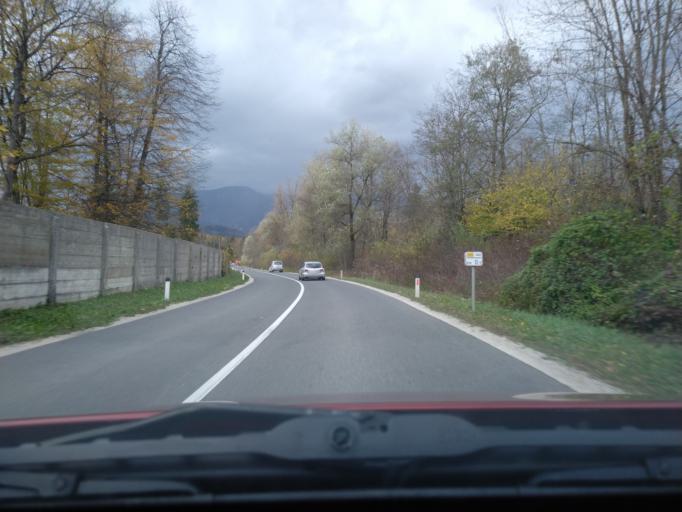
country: SI
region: Kamnik
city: Mekinje
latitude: 46.2353
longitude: 14.6092
